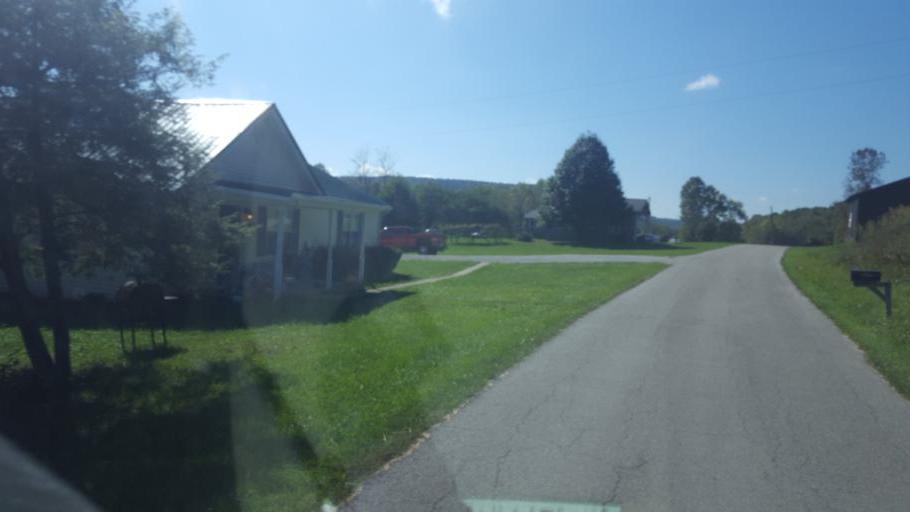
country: US
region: Kentucky
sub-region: Fleming County
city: Flemingsburg
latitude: 38.4447
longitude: -83.5541
